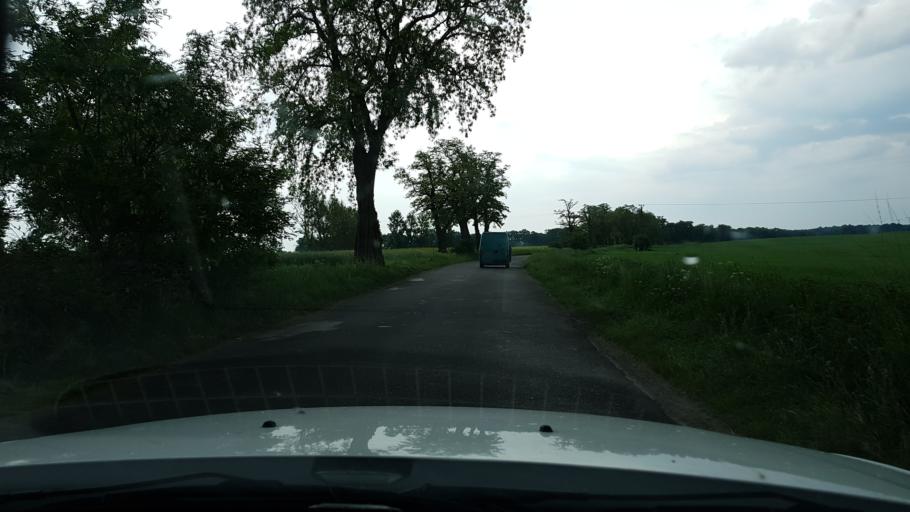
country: PL
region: West Pomeranian Voivodeship
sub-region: Powiat stargardzki
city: Marianowo
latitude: 53.3166
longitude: 15.1784
